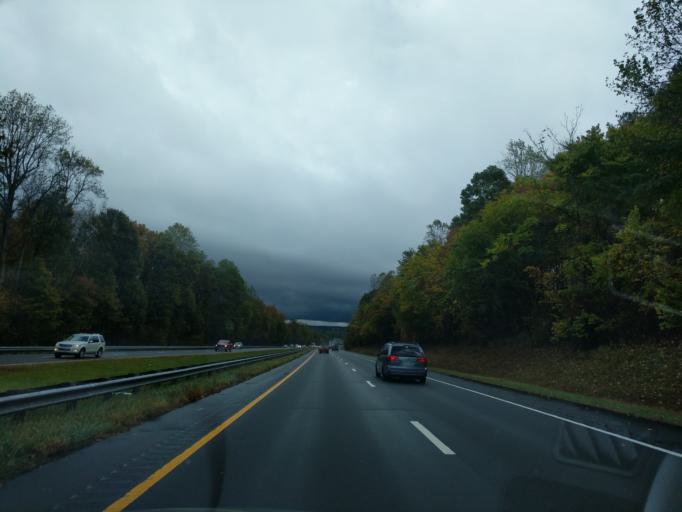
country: US
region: North Carolina
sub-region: Orange County
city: Hillsborough
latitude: 36.0459
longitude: -79.0450
